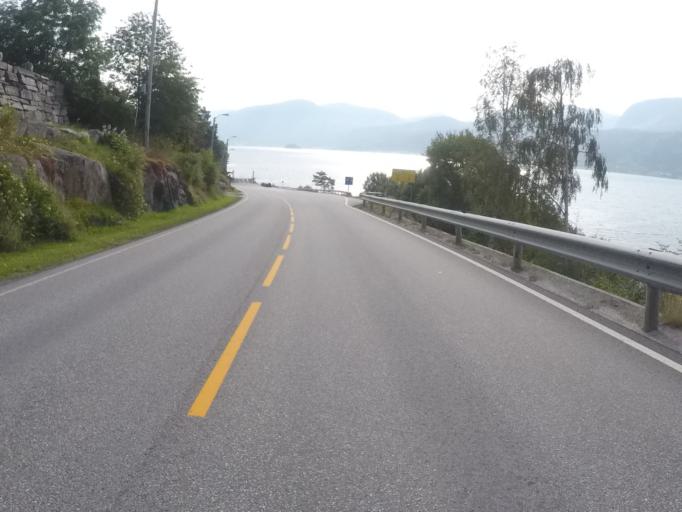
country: NO
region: More og Romsdal
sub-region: Molde
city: Hjelset
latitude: 62.6848
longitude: 7.4585
